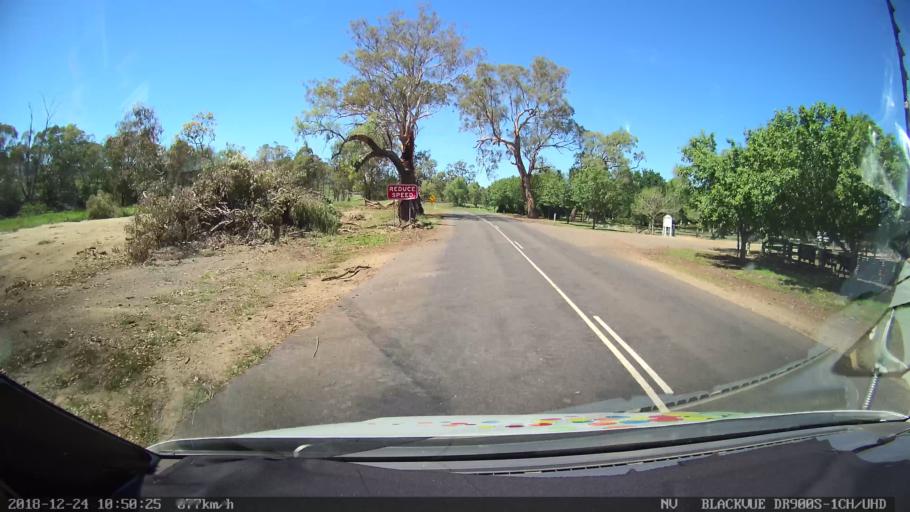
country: AU
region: New South Wales
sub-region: Upper Hunter Shire
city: Merriwa
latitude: -31.9598
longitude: 150.4240
